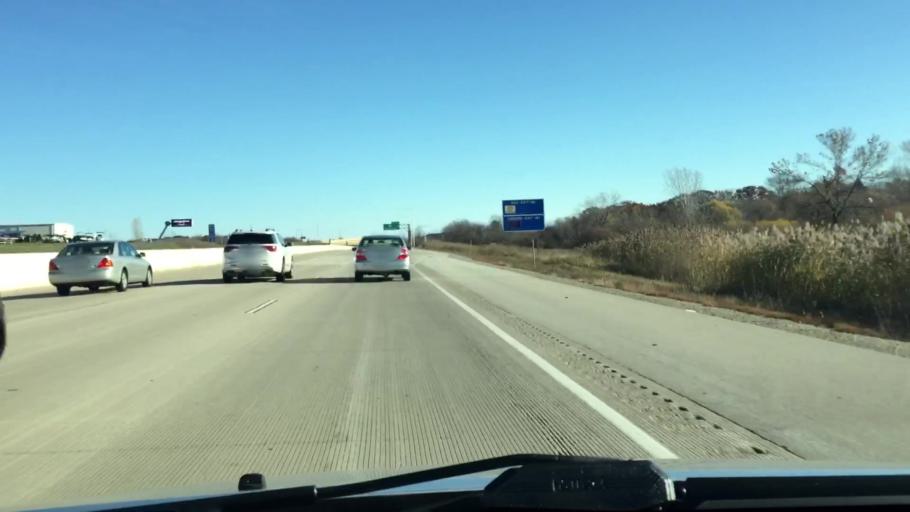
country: US
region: Wisconsin
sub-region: Brown County
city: De Pere
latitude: 44.4260
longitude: -88.1191
